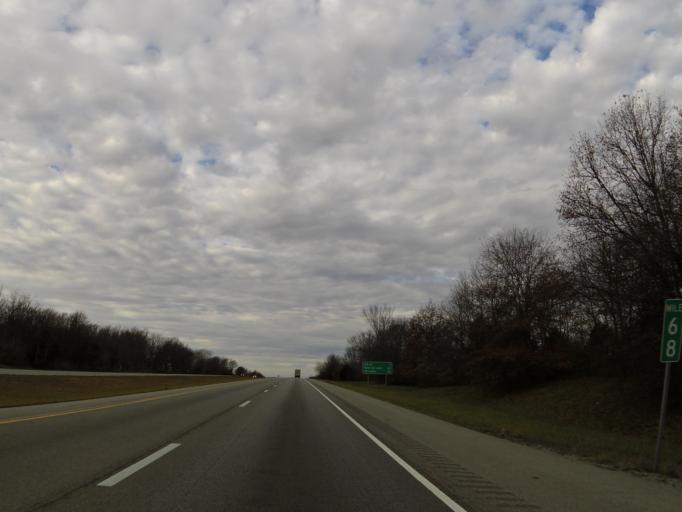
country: US
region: Illinois
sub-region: Jefferson County
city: Mount Vernon
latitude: 38.3622
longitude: -89.0492
